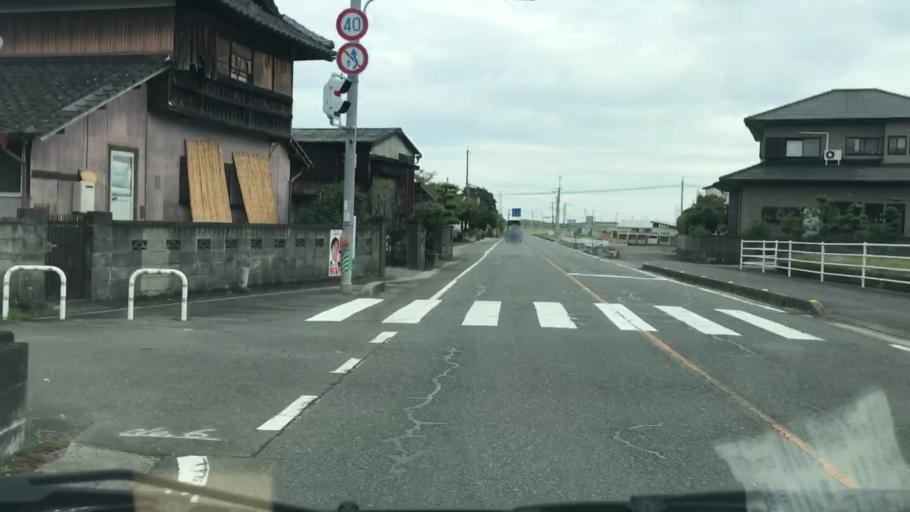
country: JP
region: Saga Prefecture
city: Saga-shi
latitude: 33.2872
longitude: 130.2503
